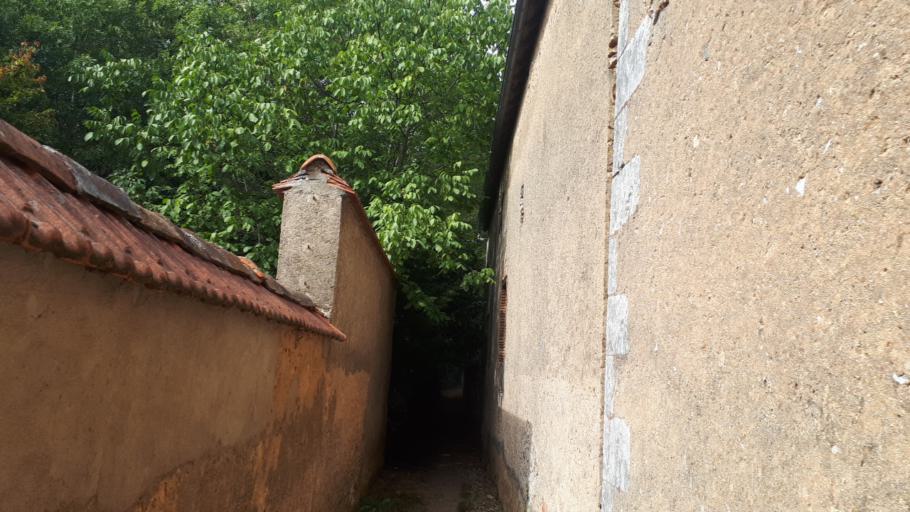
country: FR
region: Centre
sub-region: Departement du Cher
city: Henrichemont
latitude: 47.3044
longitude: 2.5268
